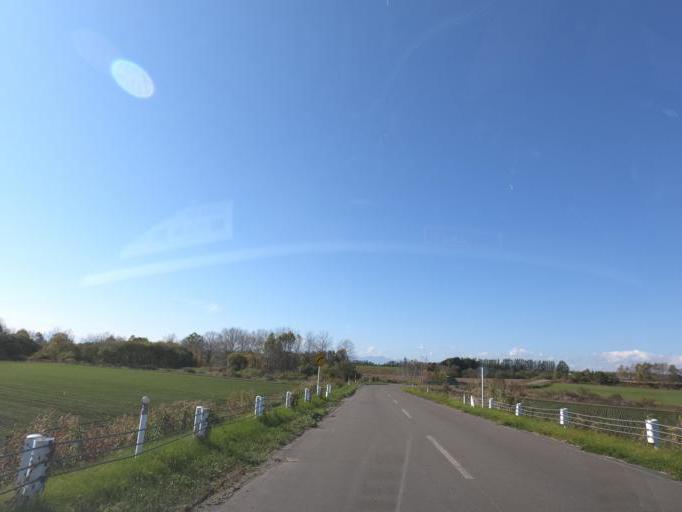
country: JP
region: Hokkaido
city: Otofuke
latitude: 43.0596
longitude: 143.2781
